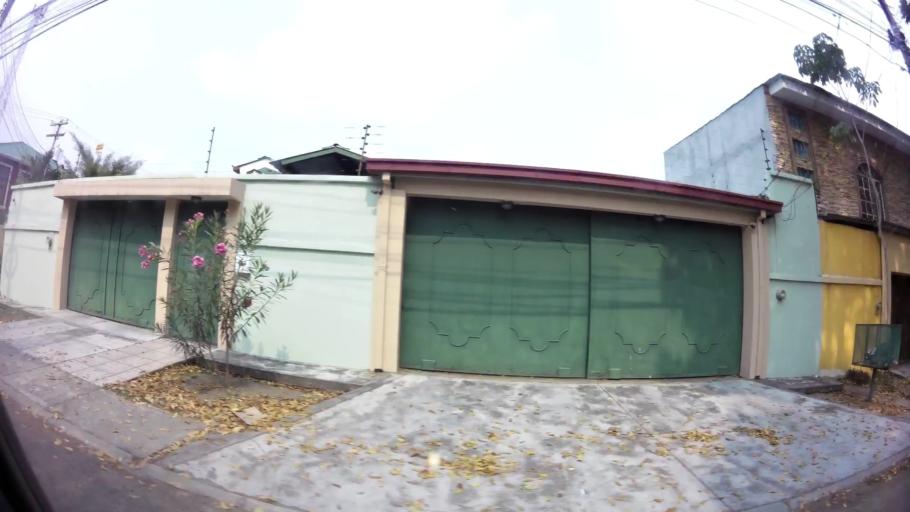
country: HN
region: Cortes
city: San Pedro Sula
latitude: 15.5271
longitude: -88.0276
